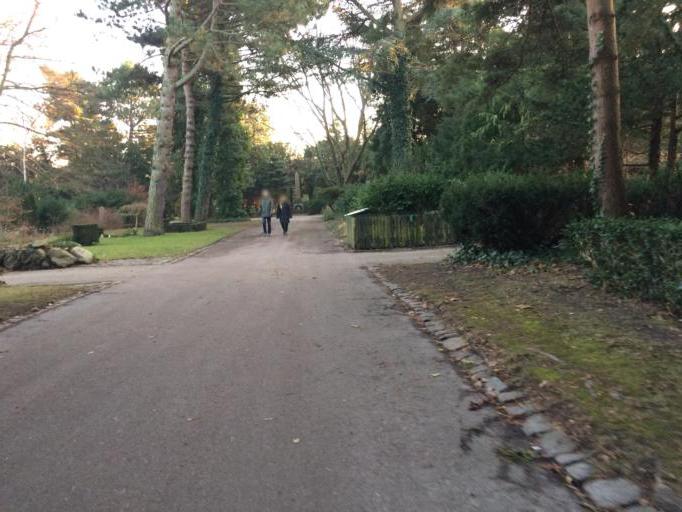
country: DK
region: Capital Region
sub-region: Frederiksberg Kommune
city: Frederiksberg
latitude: 55.6590
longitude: 12.5287
